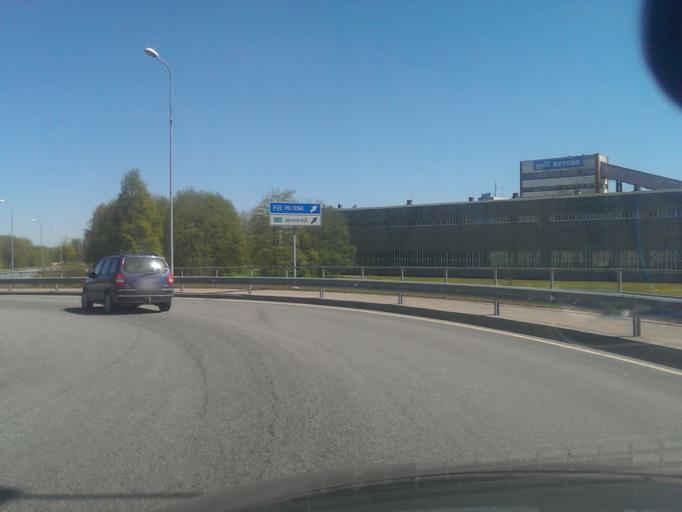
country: LV
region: Ventspils
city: Ventspils
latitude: 57.3897
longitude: 21.5911
